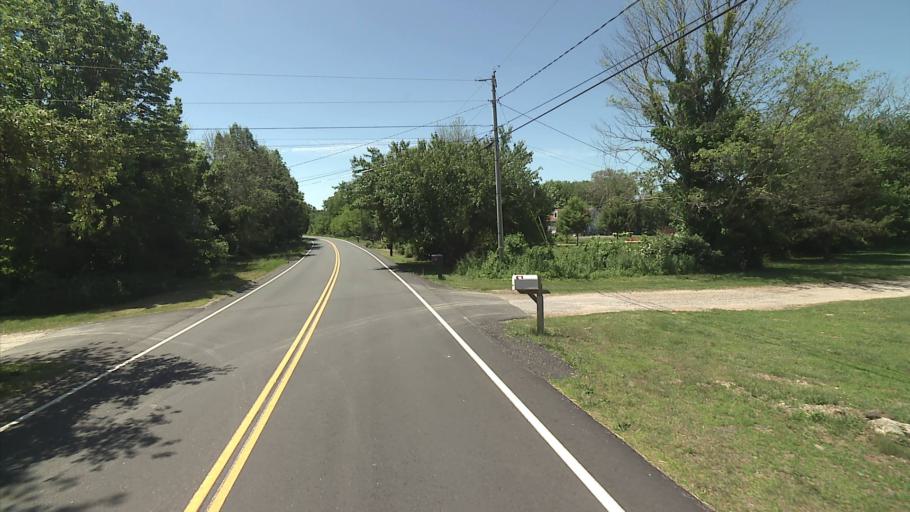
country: US
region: Connecticut
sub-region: Windham County
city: Plainfield
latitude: 41.6354
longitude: -71.8479
